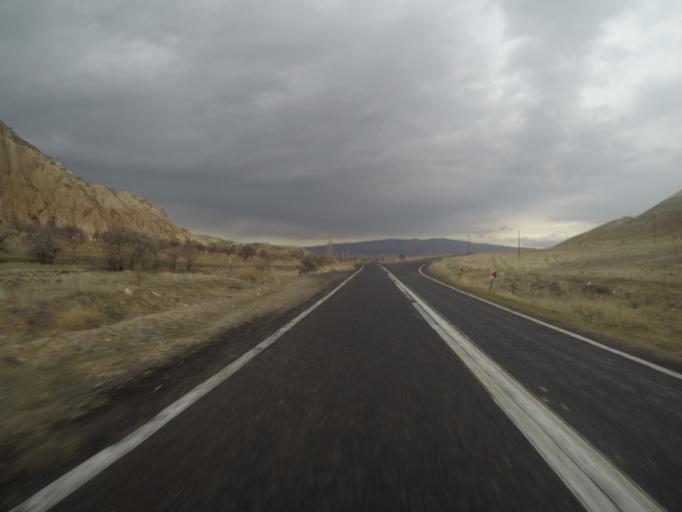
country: TR
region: Nevsehir
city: Goereme
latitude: 38.6720
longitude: 34.8629
